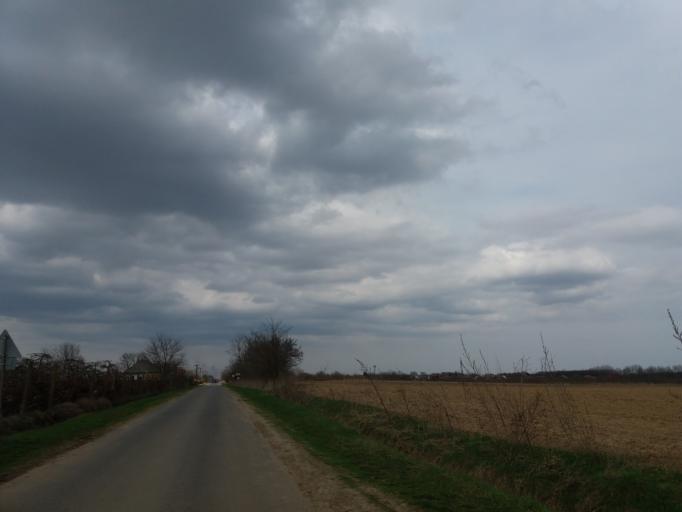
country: HU
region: Szabolcs-Szatmar-Bereg
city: Nyirtass
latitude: 48.0979
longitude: 22.0290
